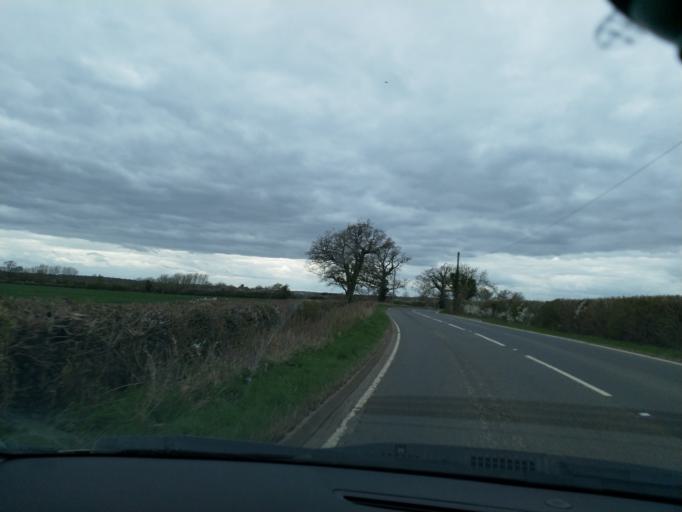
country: GB
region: England
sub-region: Warwickshire
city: Harbury
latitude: 52.1424
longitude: -1.4557
